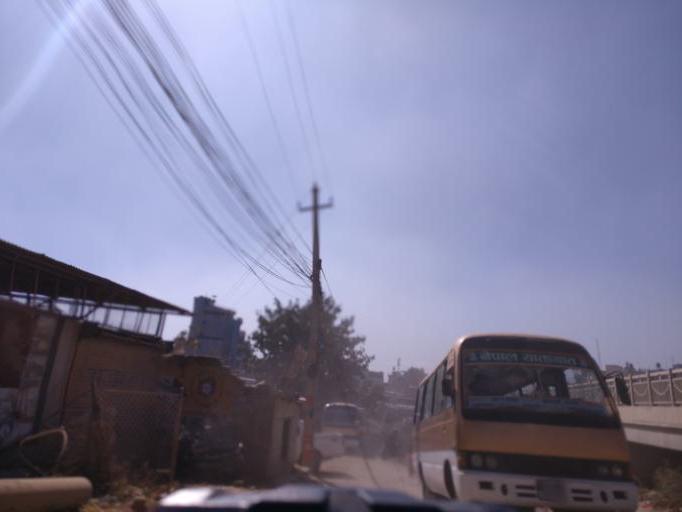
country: NP
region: Central Region
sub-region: Bagmati Zone
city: Patan
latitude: 27.6734
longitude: 85.3425
